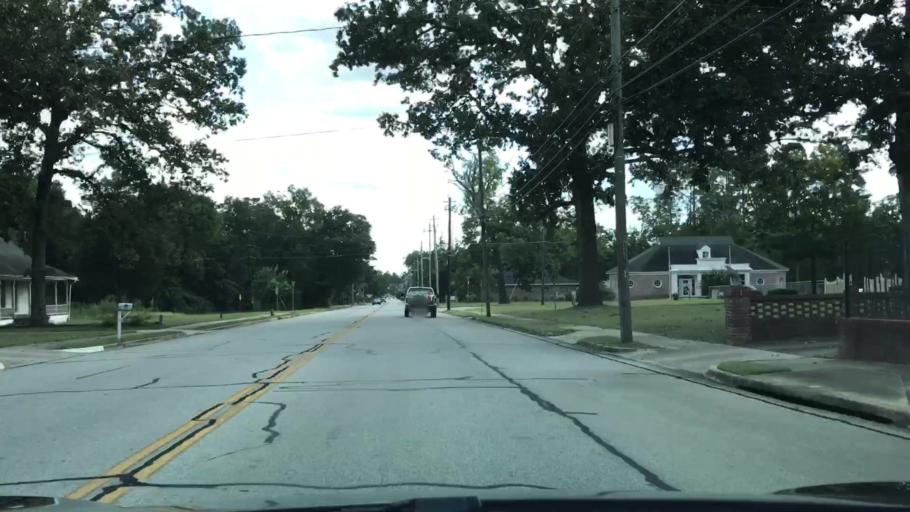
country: US
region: Georgia
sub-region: Jefferson County
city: Wadley
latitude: 32.8692
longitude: -82.4045
